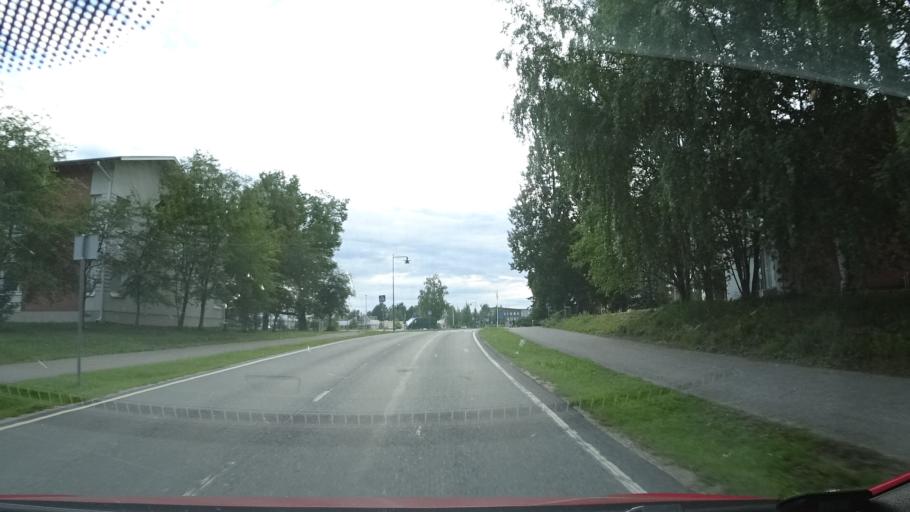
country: FI
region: Northern Ostrobothnia
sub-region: Oulu
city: Liminka
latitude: 64.8089
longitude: 25.4190
